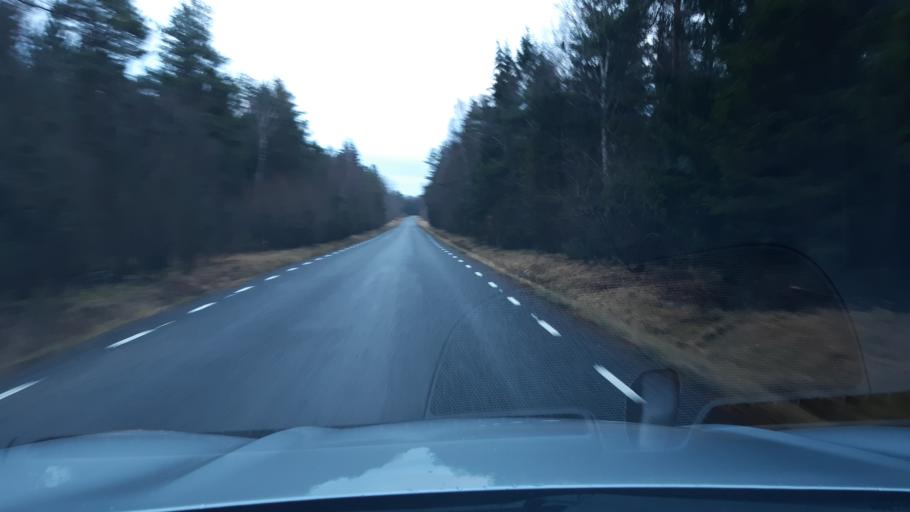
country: EE
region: Harju
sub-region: Saku vald
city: Saku
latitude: 59.1852
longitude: 24.6063
